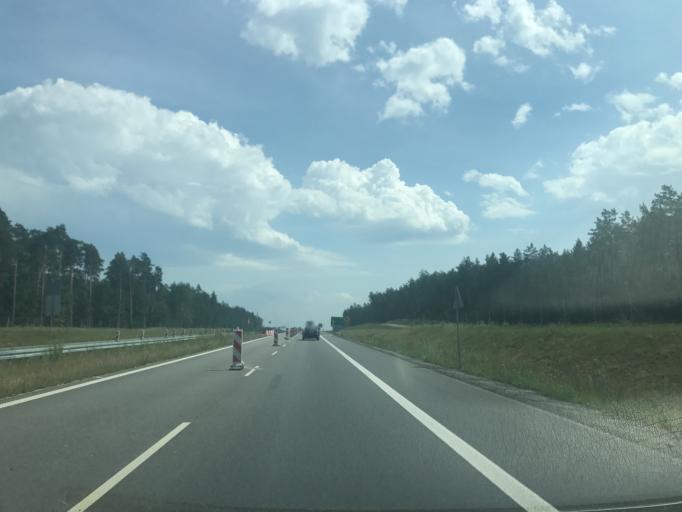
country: PL
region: Warmian-Masurian Voivodeship
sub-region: Powiat ostrodzki
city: Ostroda
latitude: 53.7335
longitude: 19.9226
